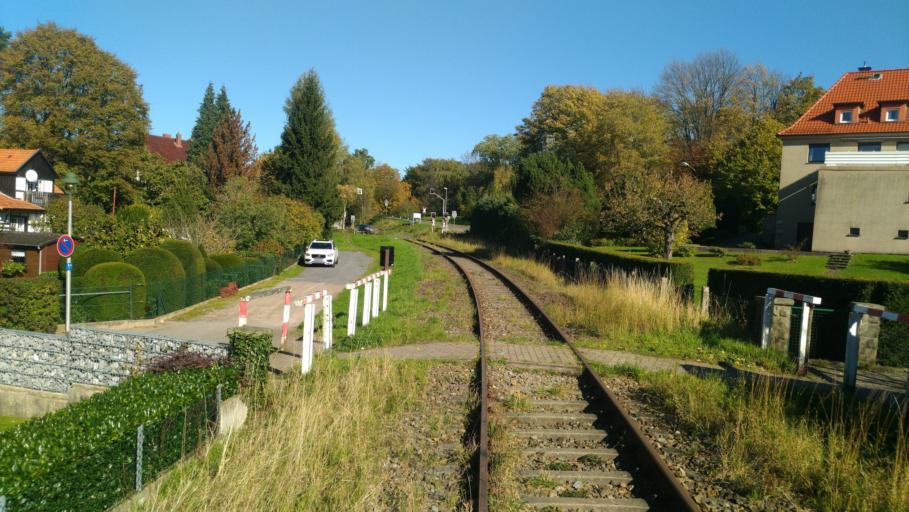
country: DE
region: Lower Saxony
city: Obernkirchen
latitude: 52.2663
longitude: 9.1318
